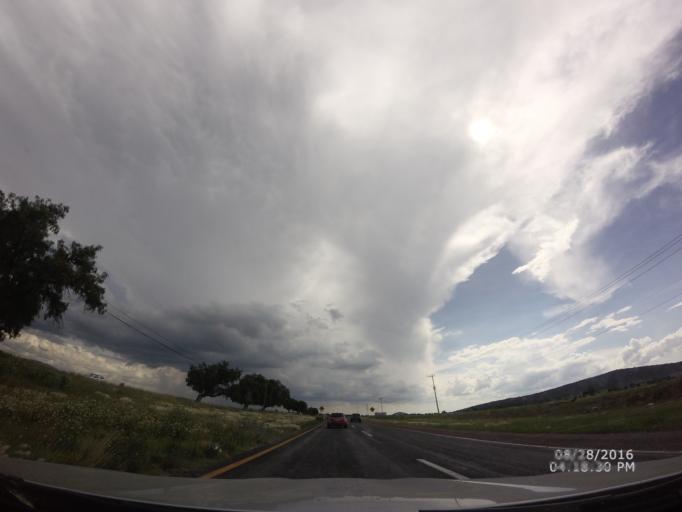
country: MX
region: Hidalgo
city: Zapotlan de Juarez
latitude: 19.9645
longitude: -98.8597
